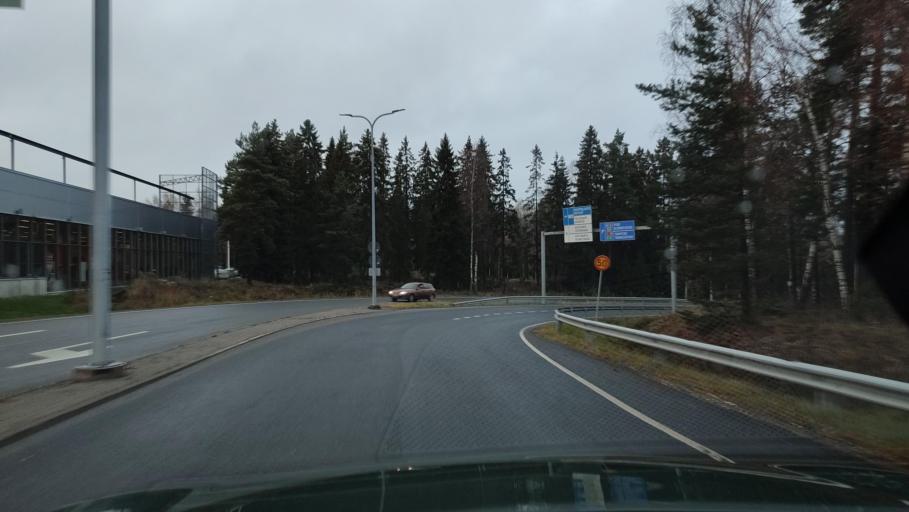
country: FI
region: Ostrobothnia
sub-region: Vaasa
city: Vaasa
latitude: 63.1015
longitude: 21.6390
